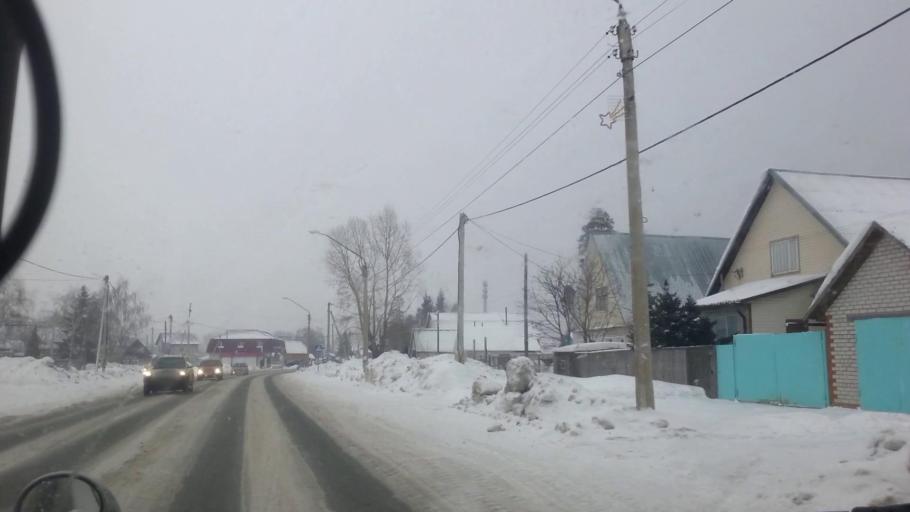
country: RU
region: Altai Krai
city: Vlasikha
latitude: 53.2929
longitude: 83.5706
